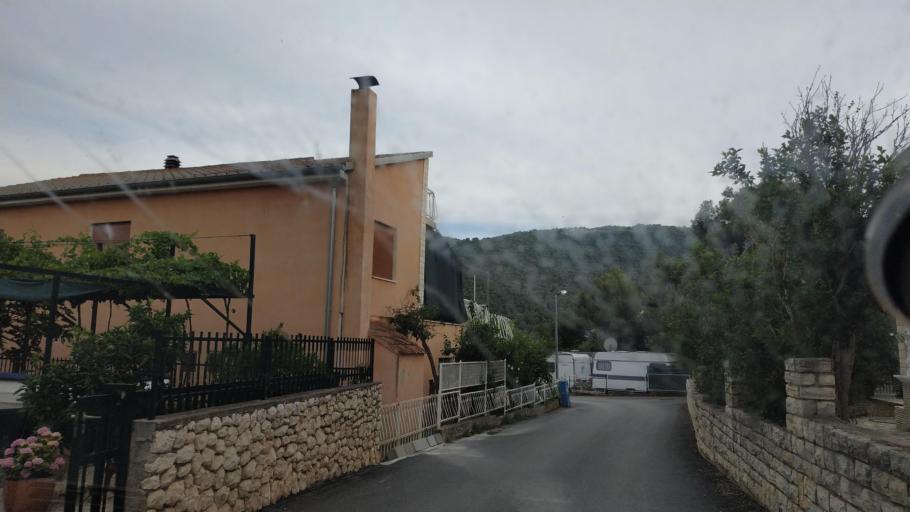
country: HR
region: Sibensko-Kniniska
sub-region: Grad Sibenik
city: Brodarica
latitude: 43.6361
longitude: 15.9618
